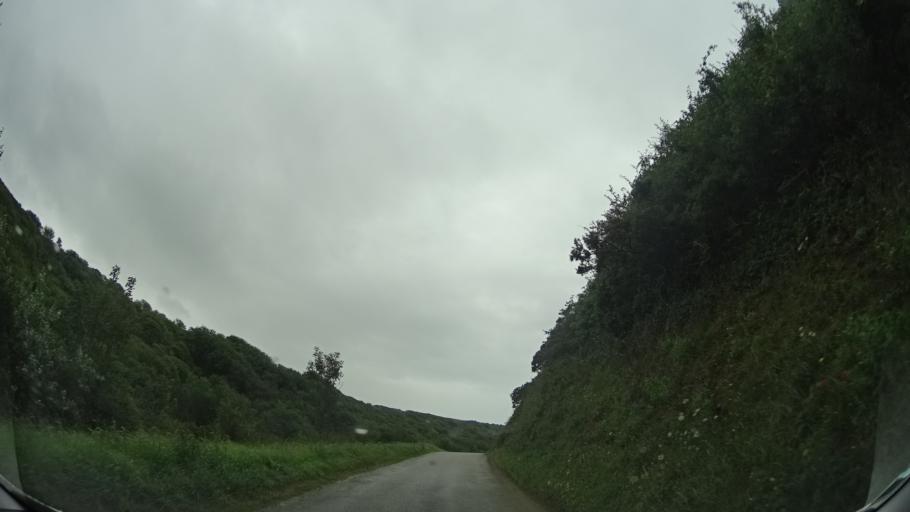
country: FR
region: Lower Normandy
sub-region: Departement de la Manche
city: Beaumont-Hague
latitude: 49.6086
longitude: -1.8254
